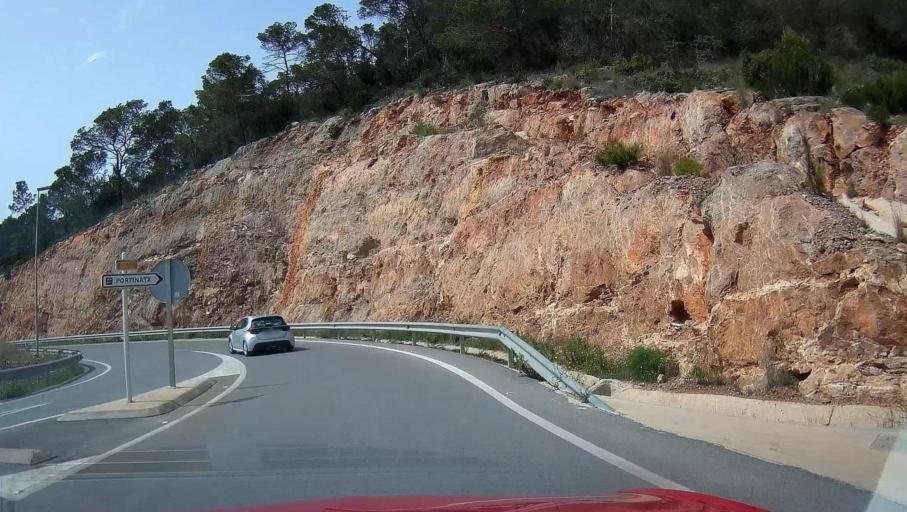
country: ES
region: Balearic Islands
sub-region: Illes Balears
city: Sant Joan de Labritja
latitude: 39.0756
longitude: 1.5062
